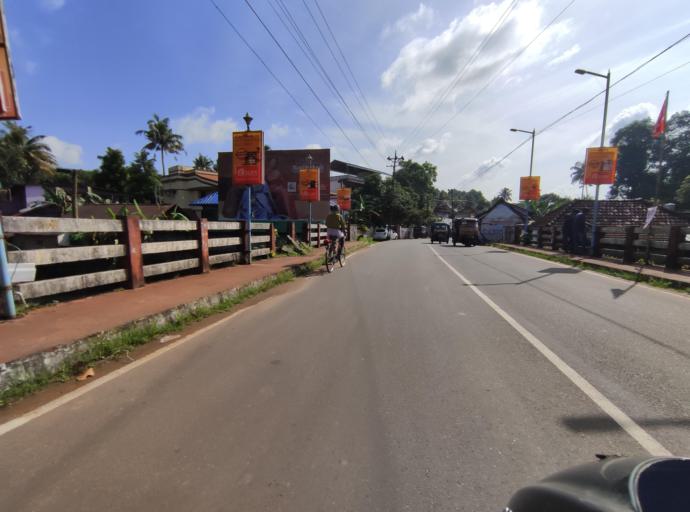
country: IN
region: Kerala
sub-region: Kottayam
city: Kottayam
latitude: 9.5841
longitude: 76.5139
